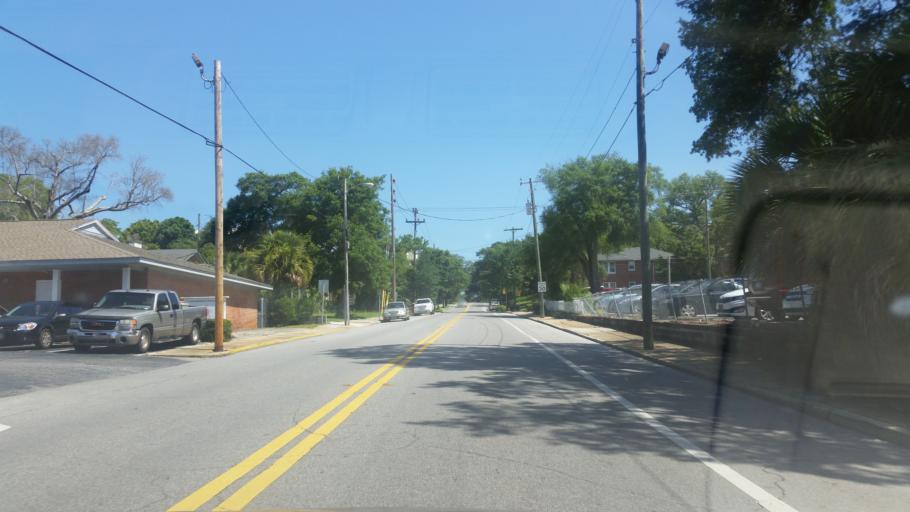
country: US
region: Florida
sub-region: Escambia County
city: Pensacola
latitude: 30.4171
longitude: -87.2192
